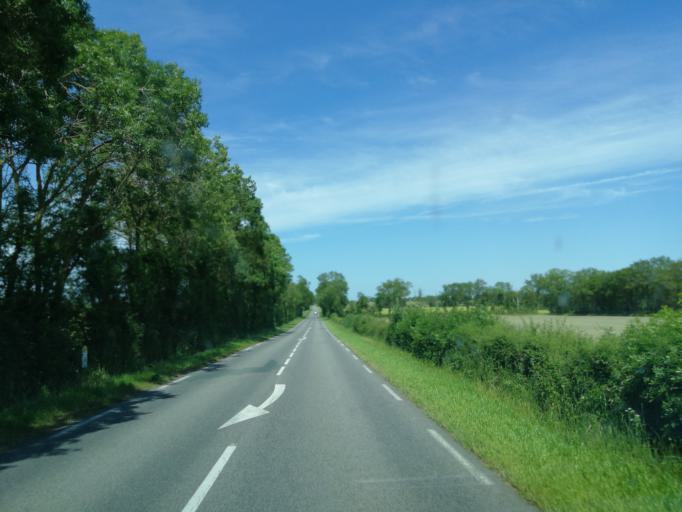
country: FR
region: Poitou-Charentes
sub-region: Departement des Deux-Sevres
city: Saint-Varent
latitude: 46.8881
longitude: -0.3097
